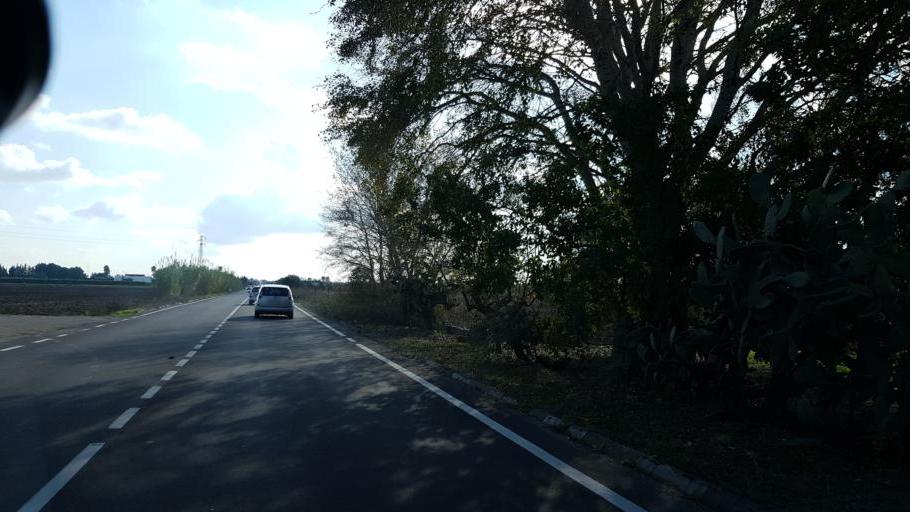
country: IT
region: Apulia
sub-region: Provincia di Lecce
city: Veglie
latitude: 40.3597
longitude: 17.9679
